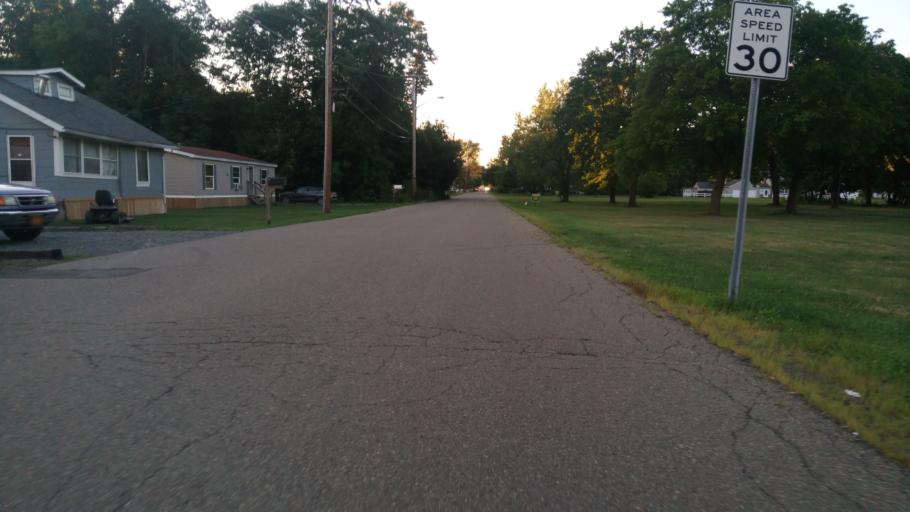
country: US
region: New York
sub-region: Chemung County
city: Southport
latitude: 42.0581
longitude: -76.7969
